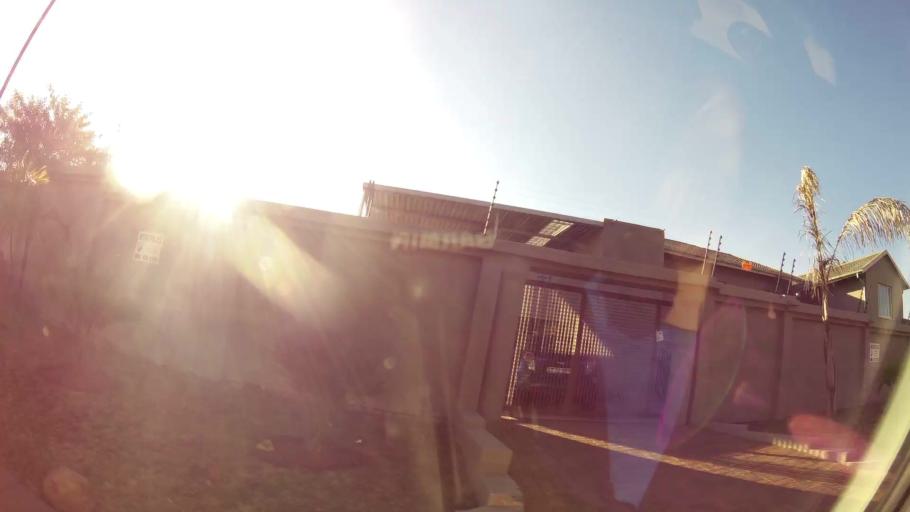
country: ZA
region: Gauteng
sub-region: City of Johannesburg Metropolitan Municipality
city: Johannesburg
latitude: -26.2702
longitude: 28.0567
